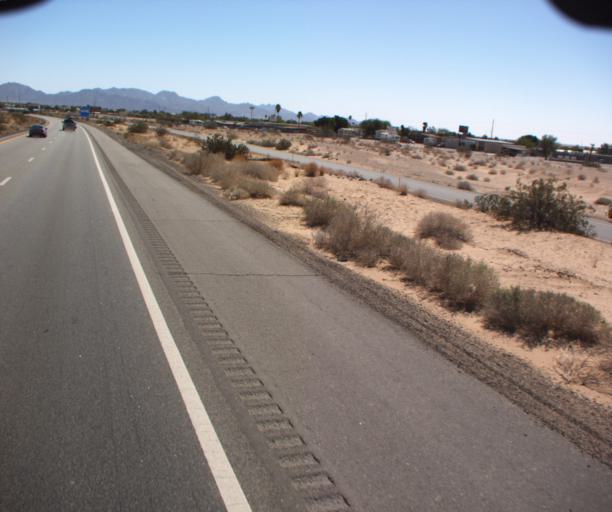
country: US
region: Arizona
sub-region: Yuma County
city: Fortuna Foothills
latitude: 32.6717
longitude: -114.4855
